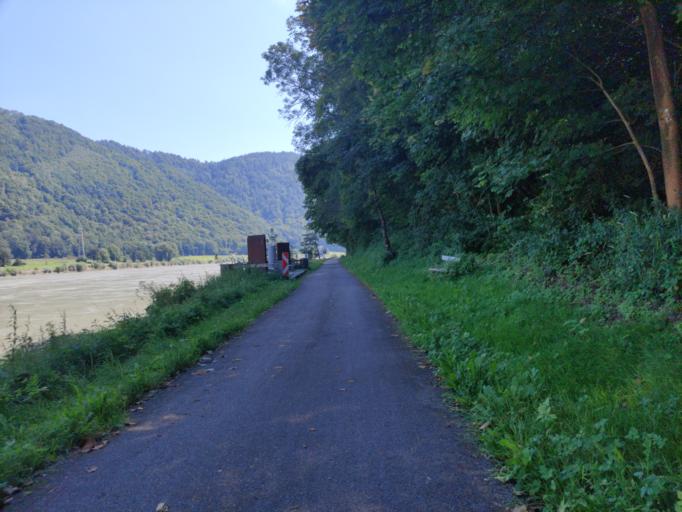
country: DE
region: Bavaria
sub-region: Lower Bavaria
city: Untergriesbach
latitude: 48.5147
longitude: 13.7139
